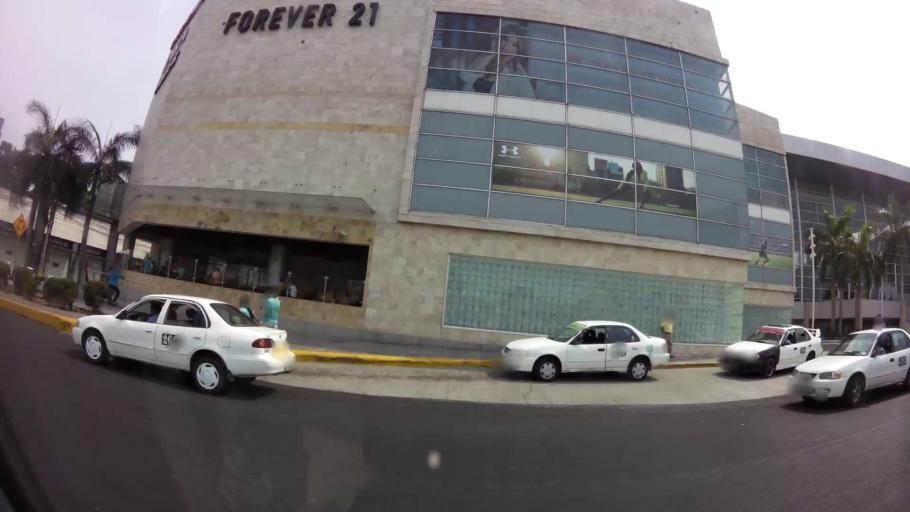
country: HN
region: Cortes
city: San Pedro Sula
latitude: 15.4971
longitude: -88.0352
